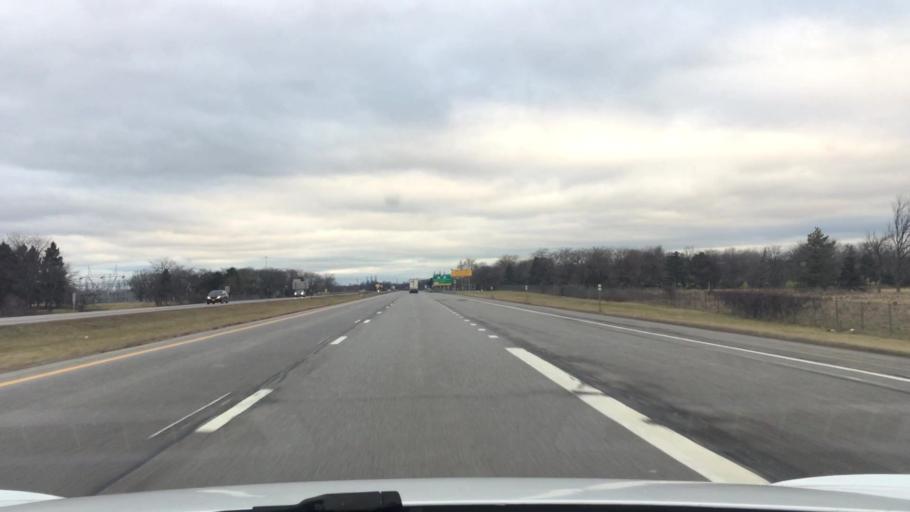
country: US
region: New York
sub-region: Niagara County
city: Lewiston
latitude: 43.1326
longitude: -79.0194
